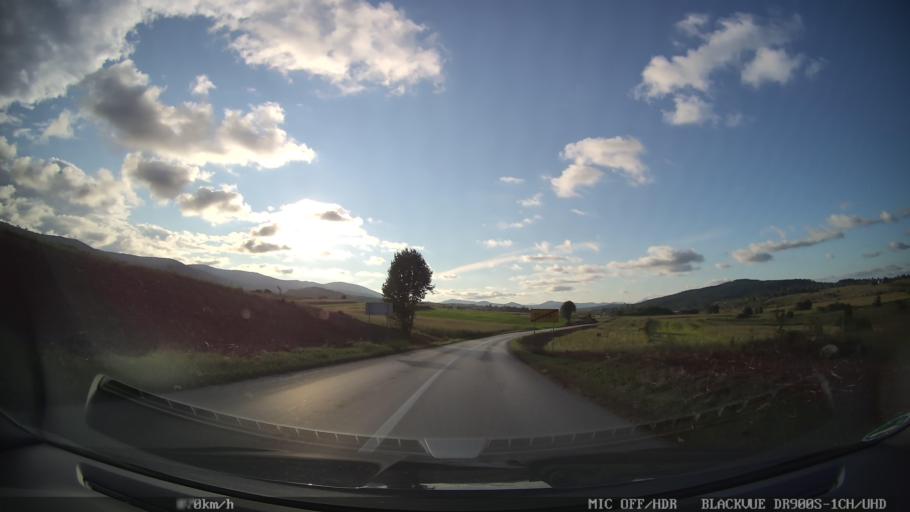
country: HR
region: Karlovacka
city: Plaski
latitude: 45.0902
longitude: 15.3617
